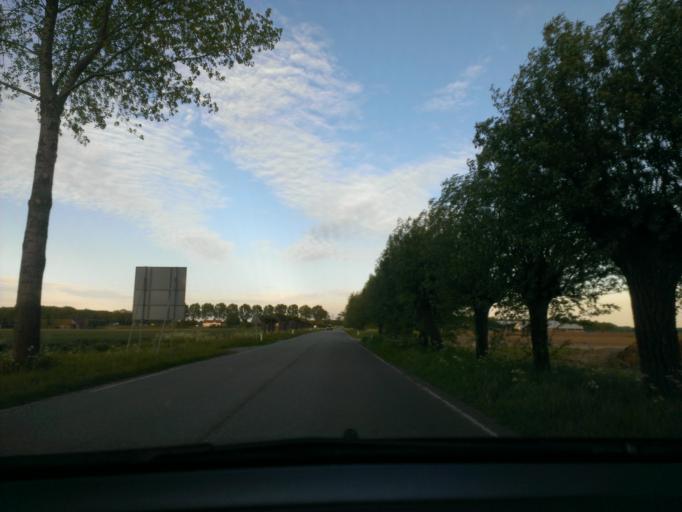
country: NL
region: South Holland
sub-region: Gemeente Oud-Beijerland
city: Oud-Beijerland
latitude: 51.7519
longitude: 4.3942
